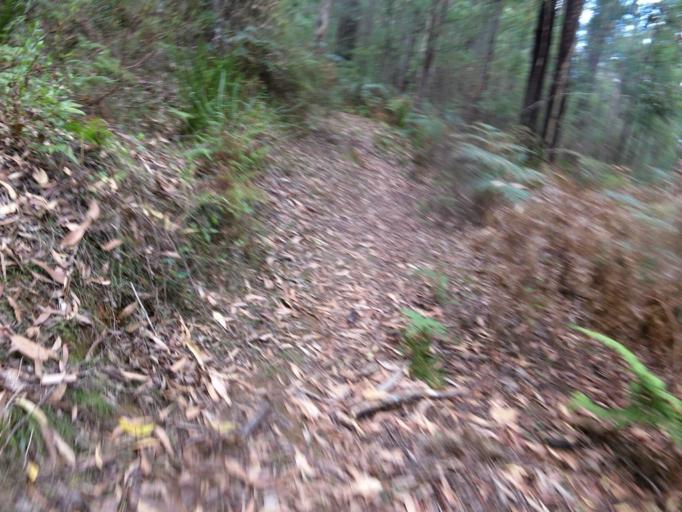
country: AU
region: Victoria
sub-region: Yarra Ranges
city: Healesville
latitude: -37.4276
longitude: 145.5755
